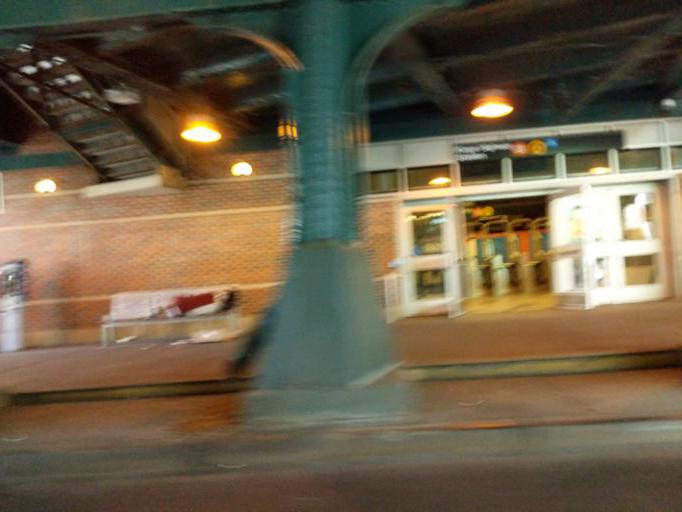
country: US
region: New York
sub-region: Kings County
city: Bensonhurst
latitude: 40.6089
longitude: -73.9578
